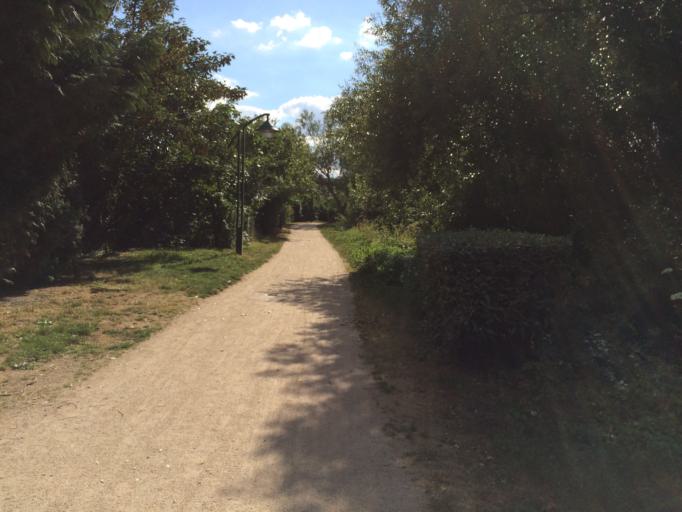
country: FR
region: Ile-de-France
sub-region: Departement de l'Essonne
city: Villebon-sur-Yvette
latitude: 48.7051
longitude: 2.2454
